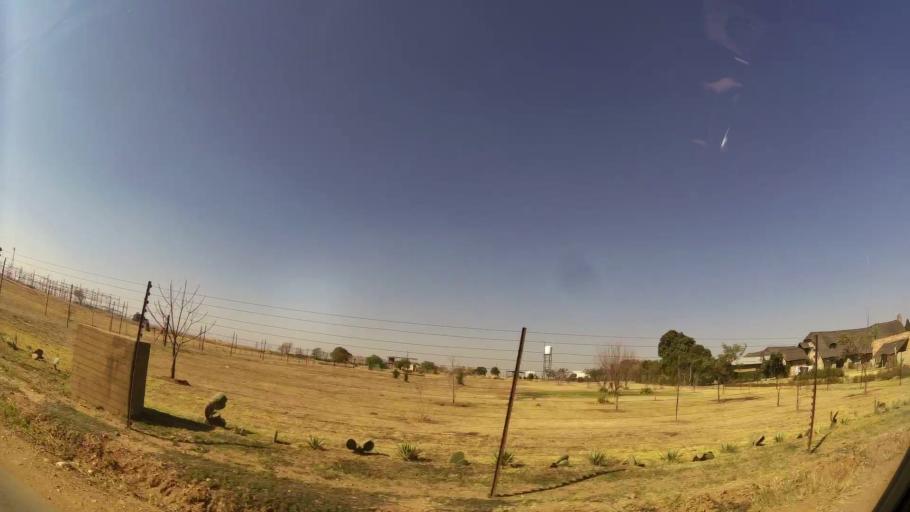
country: ZA
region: Gauteng
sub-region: City of Johannesburg Metropolitan Municipality
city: Diepsloot
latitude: -25.9254
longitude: 28.0760
